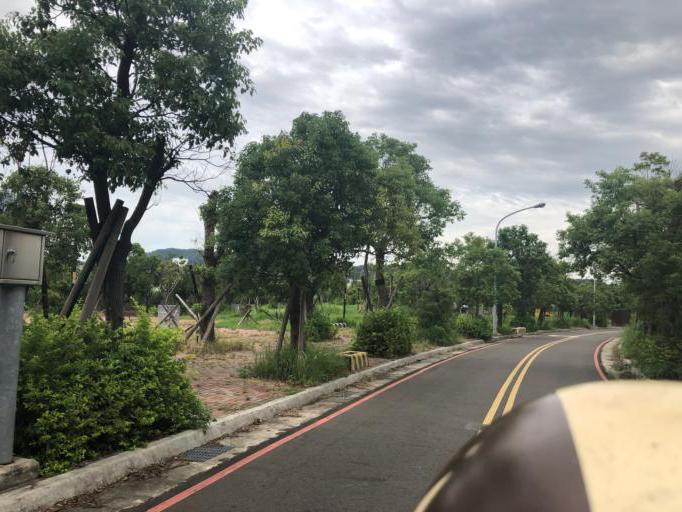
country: TW
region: Taiwan
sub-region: Hsinchu
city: Zhubei
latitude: 24.7288
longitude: 121.0942
